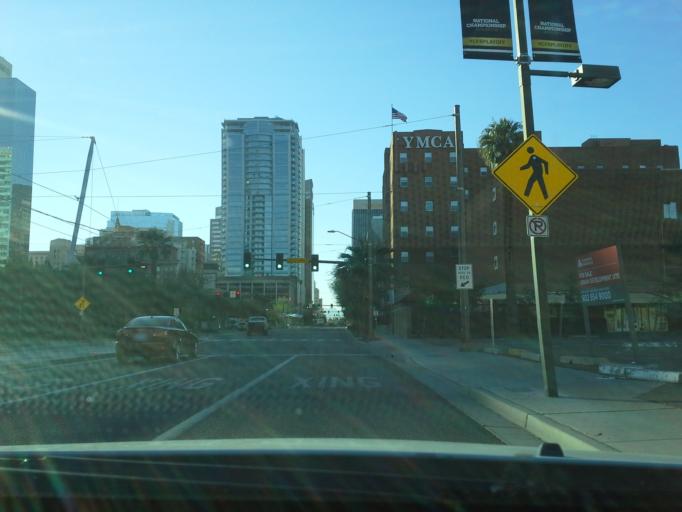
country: US
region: Arizona
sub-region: Maricopa County
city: Phoenix
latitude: 33.4540
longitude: -112.0753
